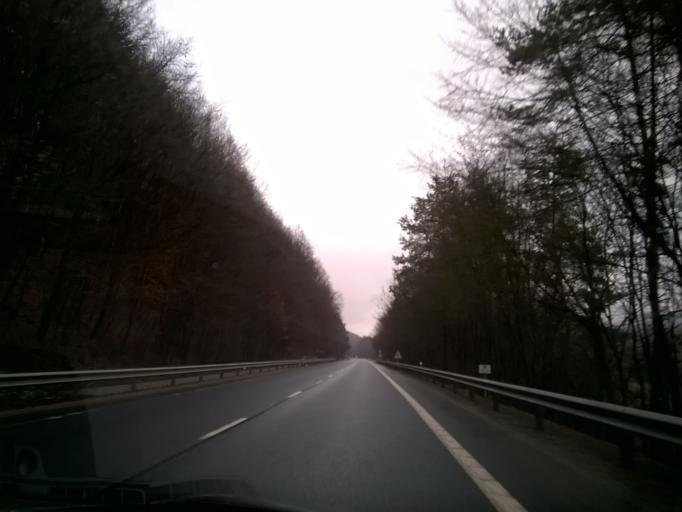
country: SK
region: Banskobystricky
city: Ziar nad Hronom
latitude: 48.6207
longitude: 18.8961
